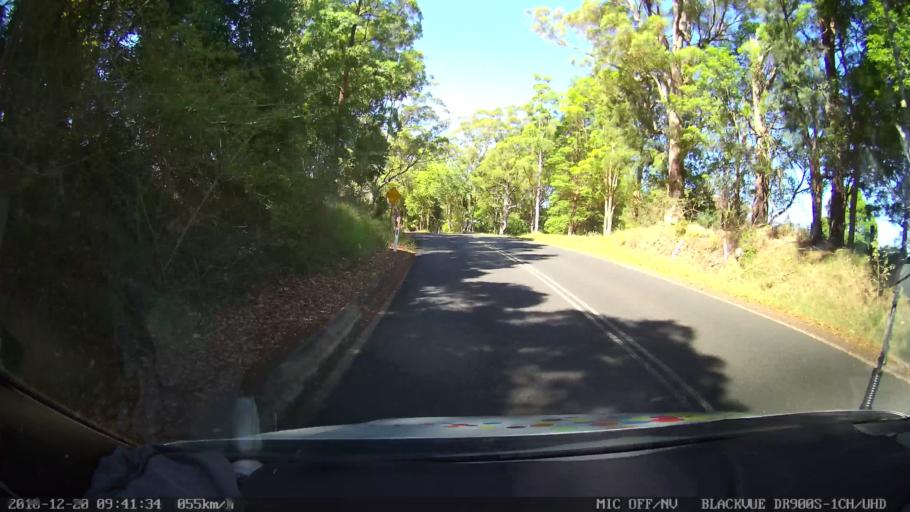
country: AU
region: New South Wales
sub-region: Lismore Municipality
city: Lismore
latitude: -28.7098
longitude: 153.2995
